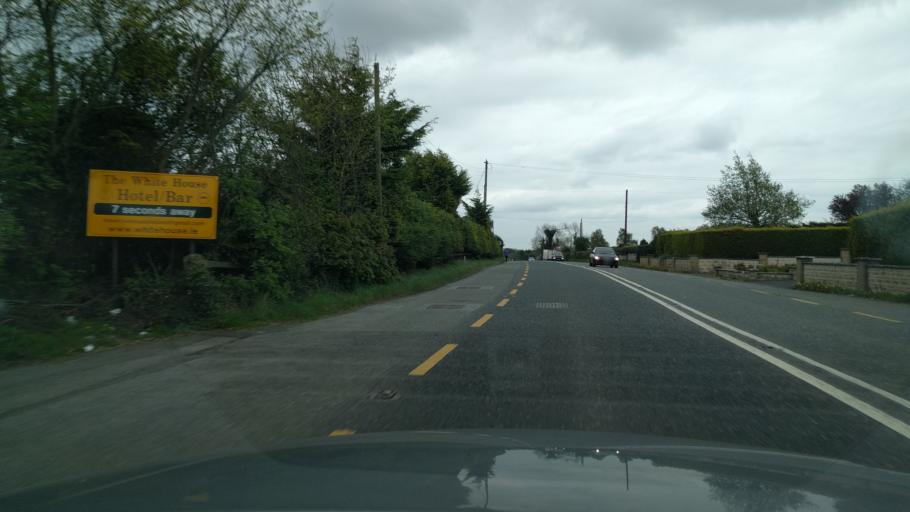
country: IE
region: Leinster
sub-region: Fingal County
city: Blanchardstown
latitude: 53.4417
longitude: -6.3393
